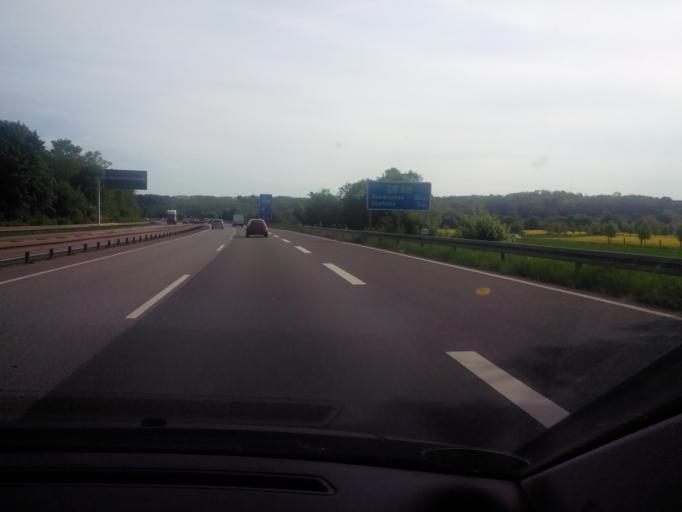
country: DE
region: Saarland
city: Wallerfangen
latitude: 49.3167
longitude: 6.7302
